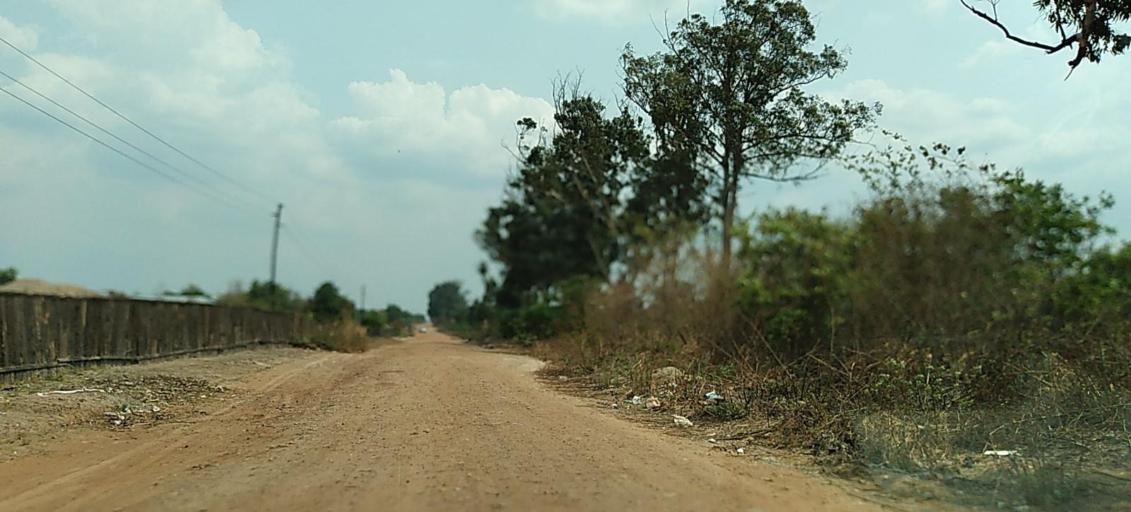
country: ZM
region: Copperbelt
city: Kalulushi
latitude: -12.8339
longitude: 28.0774
